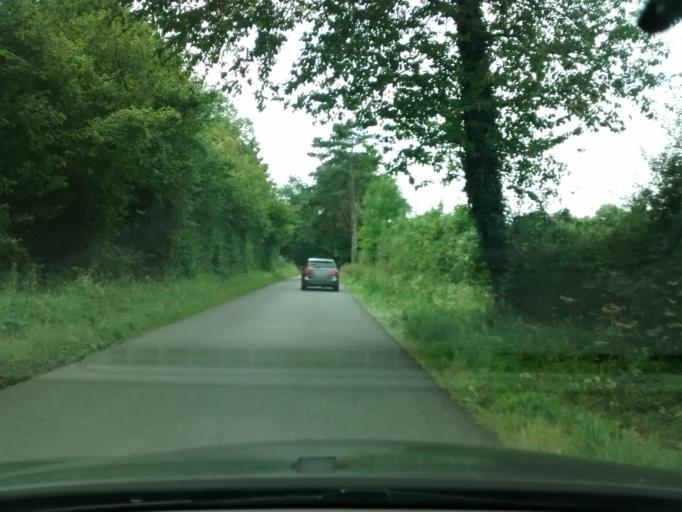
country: FR
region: Lower Normandy
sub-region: Departement du Calvados
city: Deauville
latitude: 49.3352
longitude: 0.0715
